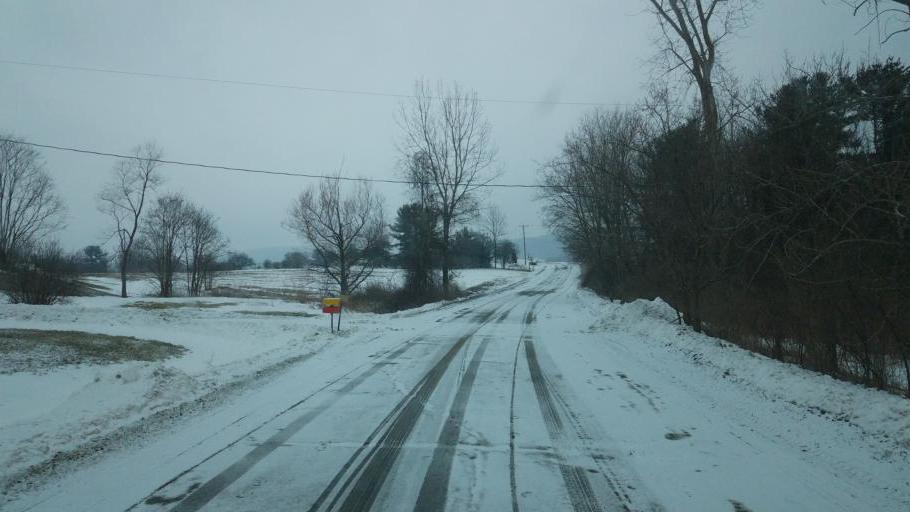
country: US
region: Pennsylvania
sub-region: Tioga County
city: Westfield
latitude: 42.1081
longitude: -77.4733
